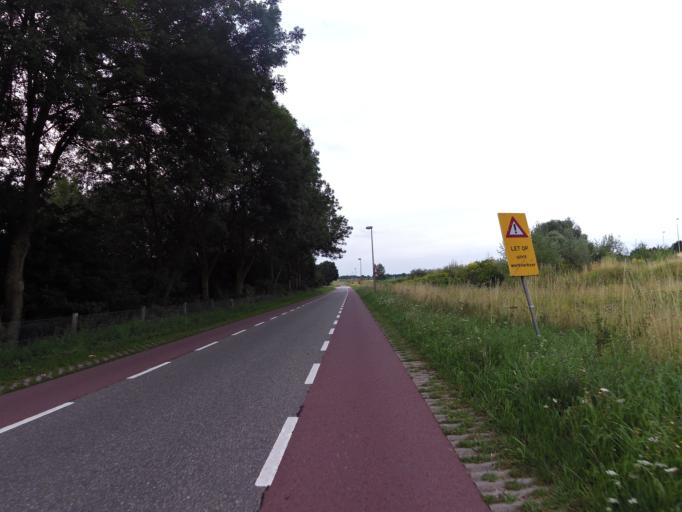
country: NL
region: Gelderland
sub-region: Gemeente Doesburg
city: Doesburg
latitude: 52.0051
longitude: 6.1532
